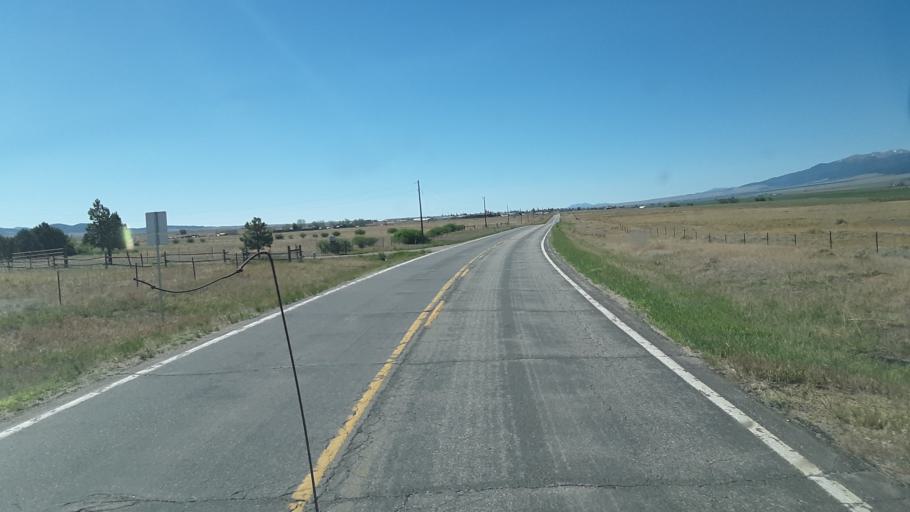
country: US
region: Colorado
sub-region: Custer County
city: Westcliffe
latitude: 38.1627
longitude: -105.4836
